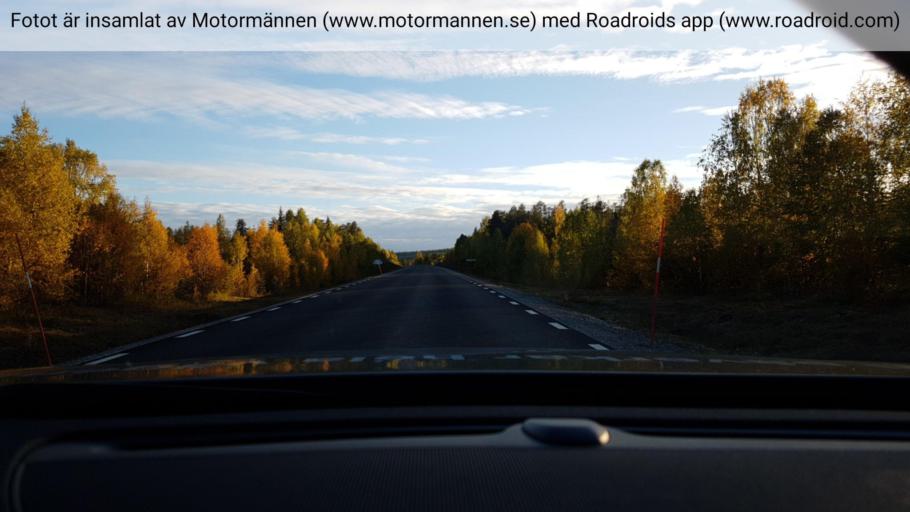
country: SE
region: Norrbotten
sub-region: Jokkmokks Kommun
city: Jokkmokk
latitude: 66.5982
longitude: 19.8115
